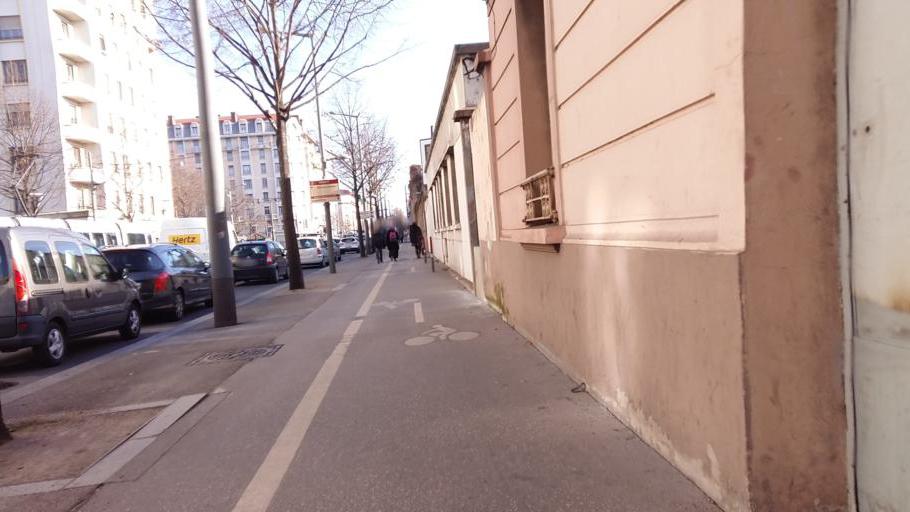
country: FR
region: Rhone-Alpes
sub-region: Departement du Rhone
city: Lyon
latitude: 45.7456
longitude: 4.8403
